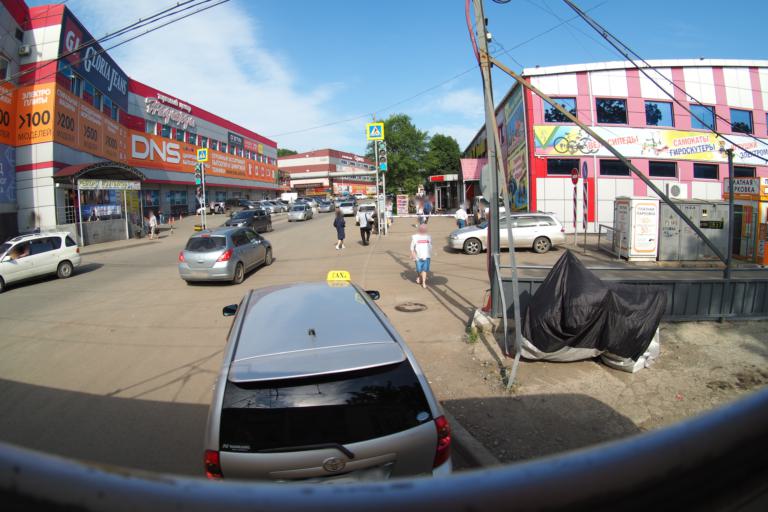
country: RU
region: Primorskiy
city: Vladivostok
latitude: 43.1073
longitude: 131.9395
